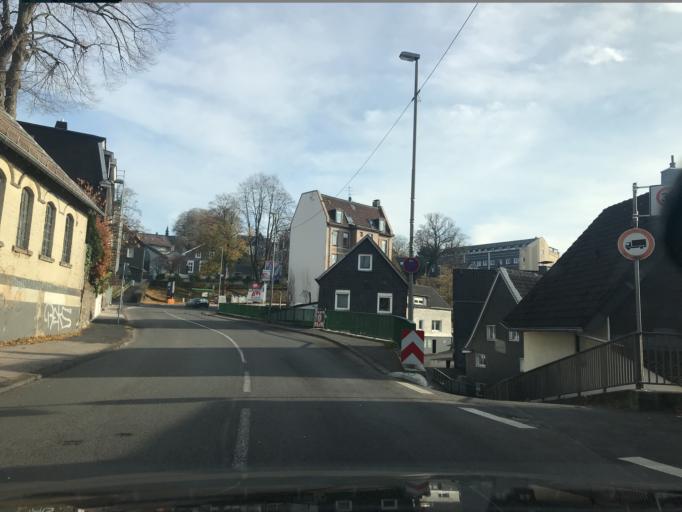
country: DE
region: North Rhine-Westphalia
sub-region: Regierungsbezirk Dusseldorf
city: Remscheid
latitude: 51.1976
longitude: 7.1636
